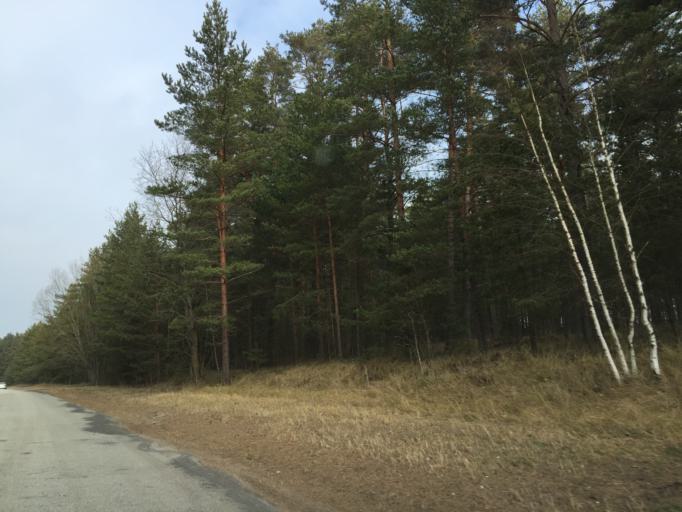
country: LV
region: Salacgrivas
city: Ainazi
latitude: 57.9313
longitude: 24.3920
